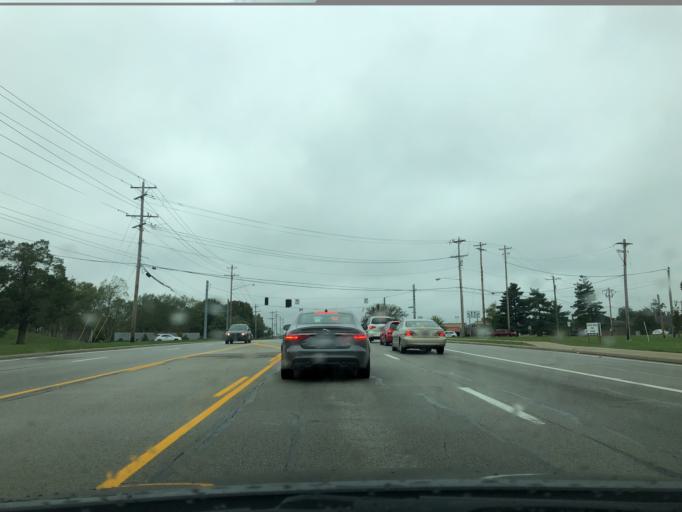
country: US
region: Ohio
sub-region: Hamilton County
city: Sixteen Mile Stand
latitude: 39.2655
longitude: -84.3336
